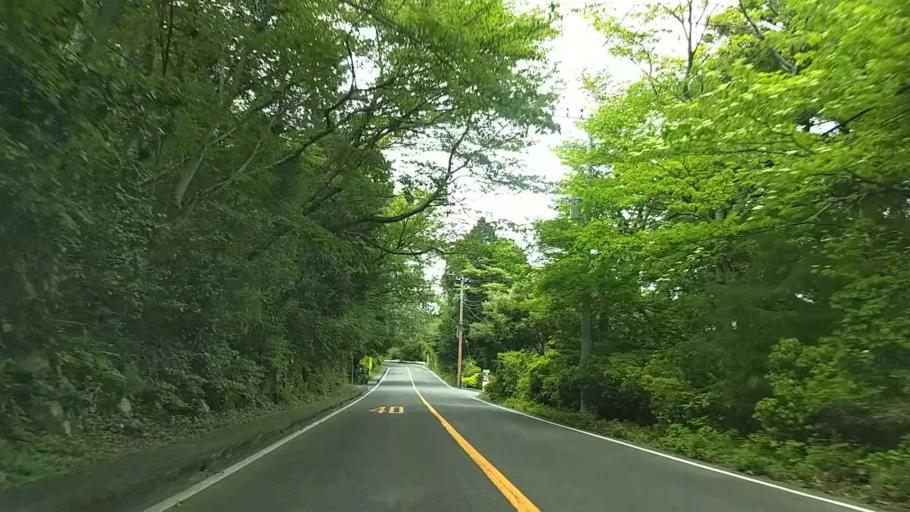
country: JP
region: Kanagawa
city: Hakone
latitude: 35.2428
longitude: 139.0437
